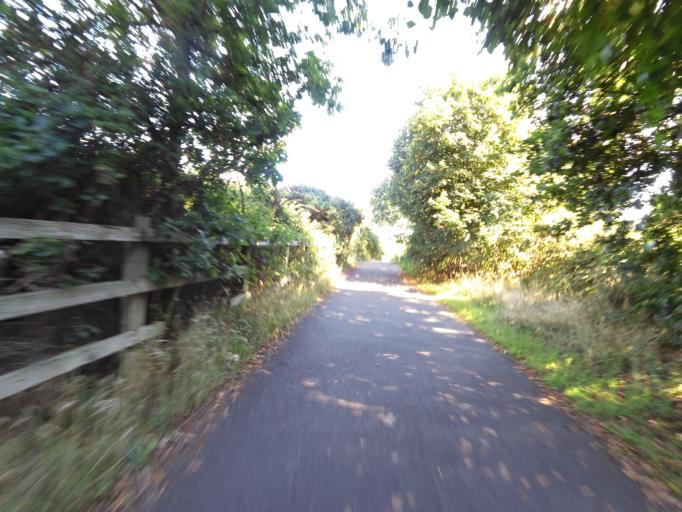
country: GB
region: England
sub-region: Suffolk
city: Kesgrave
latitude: 52.0668
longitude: 1.2736
